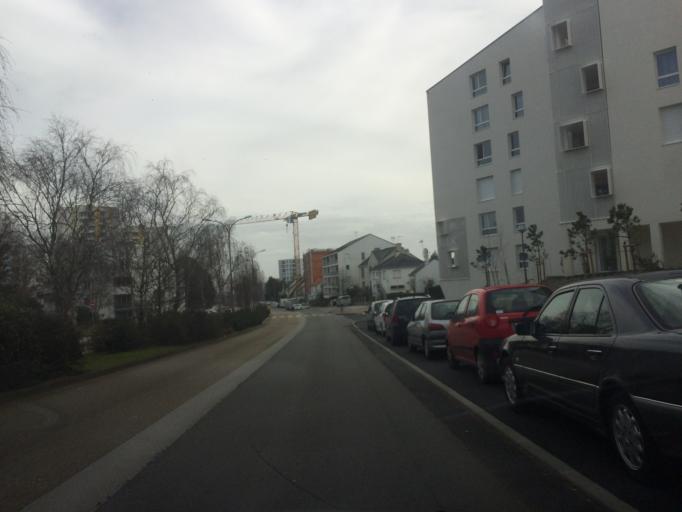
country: FR
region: Pays de la Loire
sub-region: Departement de la Loire-Atlantique
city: Saint-Nazaire
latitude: 47.2699
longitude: -2.2392
